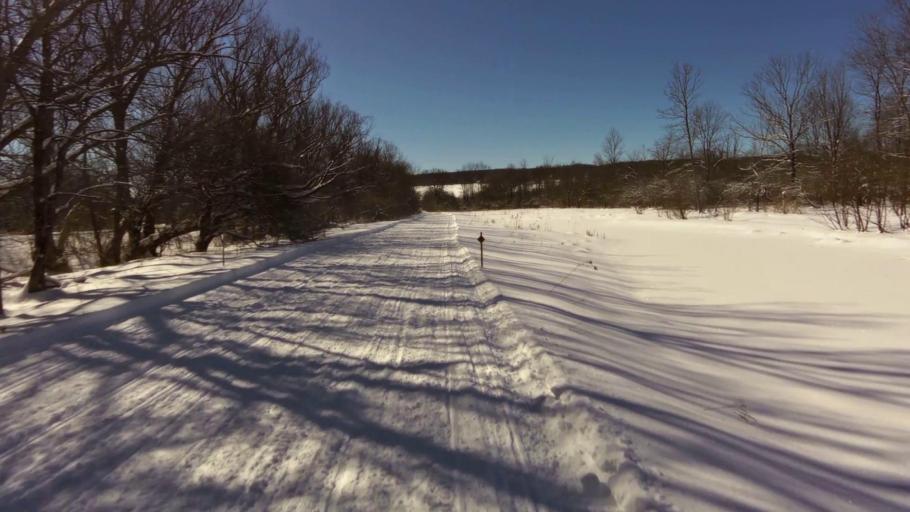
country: US
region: New York
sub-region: Chautauqua County
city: Celoron
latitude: 42.2352
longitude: -79.2934
